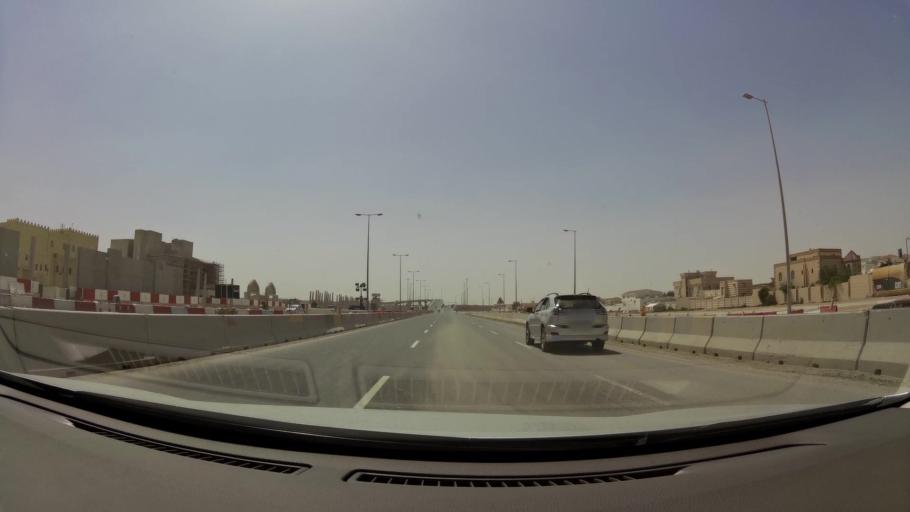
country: QA
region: Baladiyat Umm Salal
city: Umm Salal Muhammad
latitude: 25.3691
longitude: 51.4555
